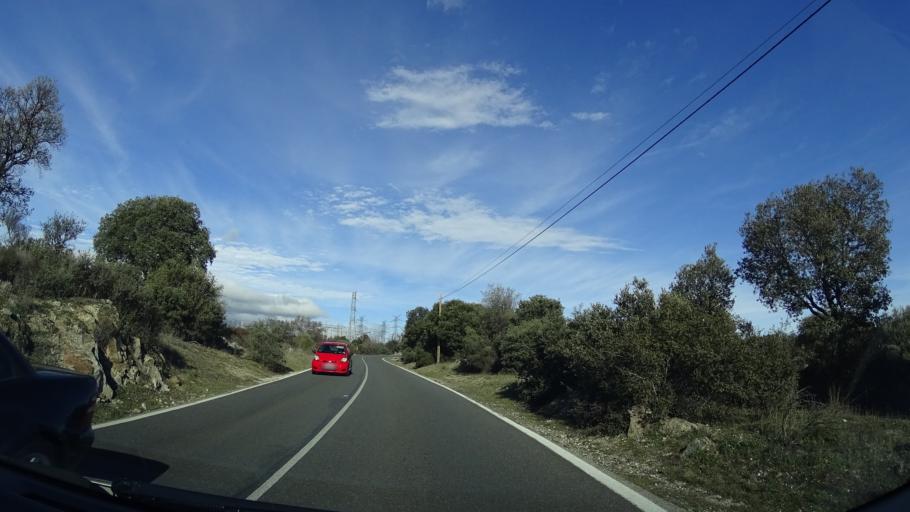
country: ES
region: Madrid
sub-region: Provincia de Madrid
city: Galapagar
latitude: 40.5938
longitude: -4.0019
